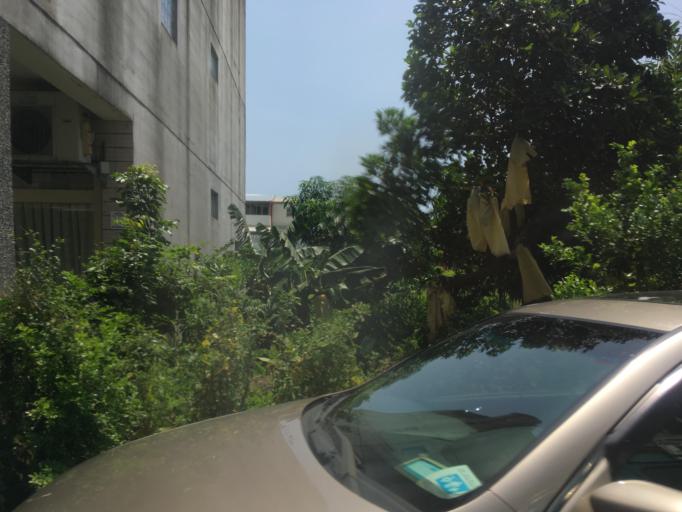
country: TW
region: Taiwan
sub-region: Yilan
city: Yilan
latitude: 24.6840
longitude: 121.7952
